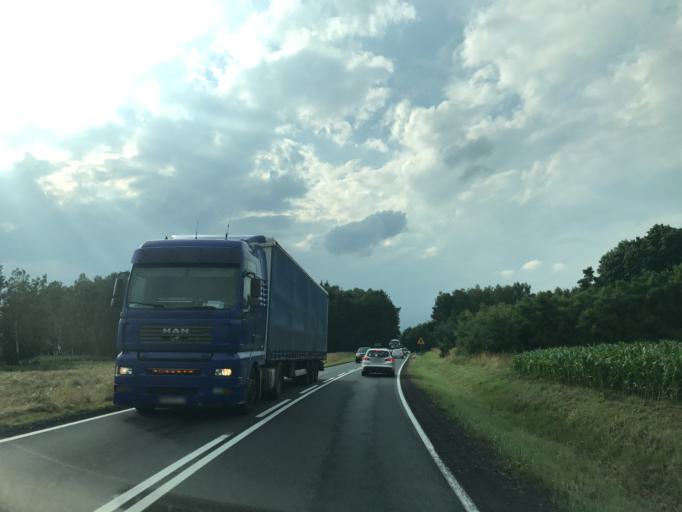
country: PL
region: Pomeranian Voivodeship
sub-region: Powiat czluchowski
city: Przechlewo
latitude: 53.7237
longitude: 17.2387
